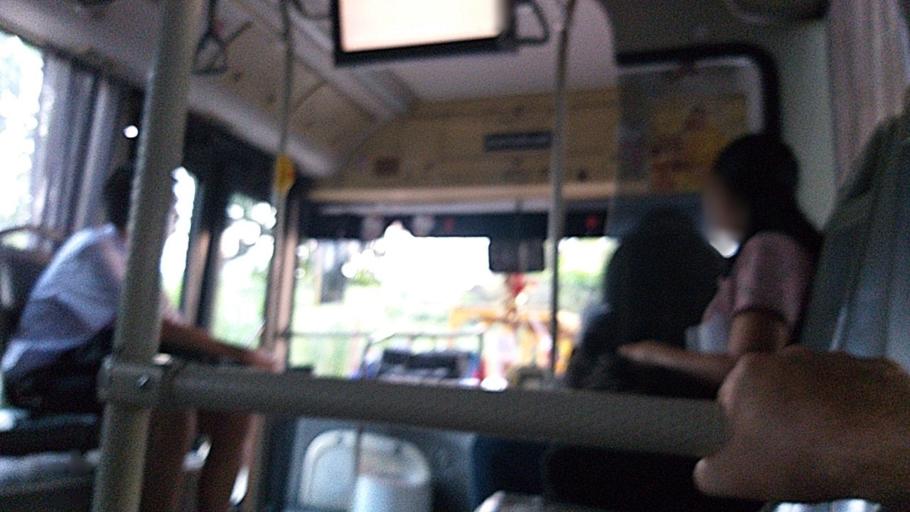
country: TH
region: Bangkok
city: Don Mueang
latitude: 13.9414
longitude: 100.6146
